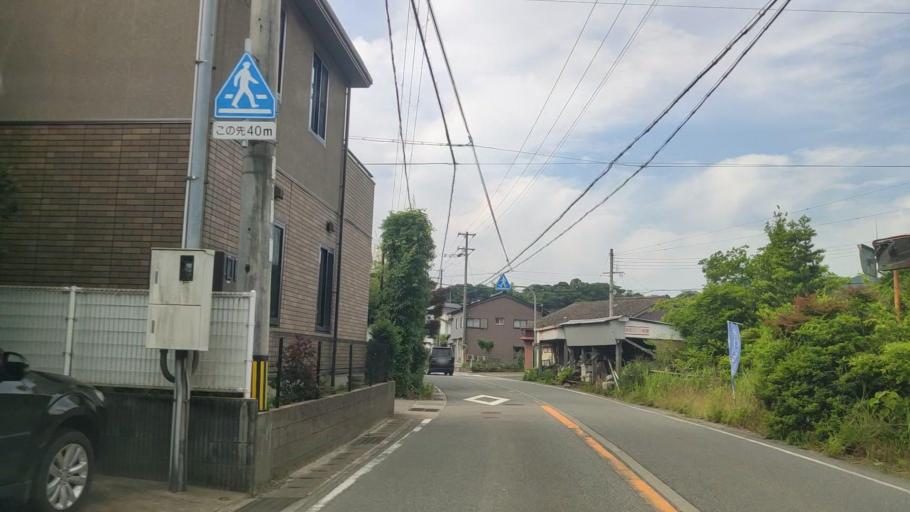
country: JP
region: Hyogo
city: Toyooka
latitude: 35.6317
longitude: 134.8164
